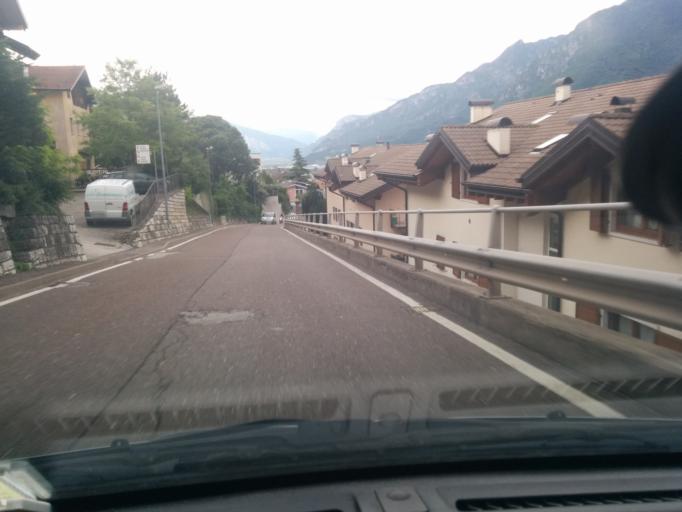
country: IT
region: Trentino-Alto Adige
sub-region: Provincia di Trento
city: Trento
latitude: 46.0846
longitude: 11.1281
